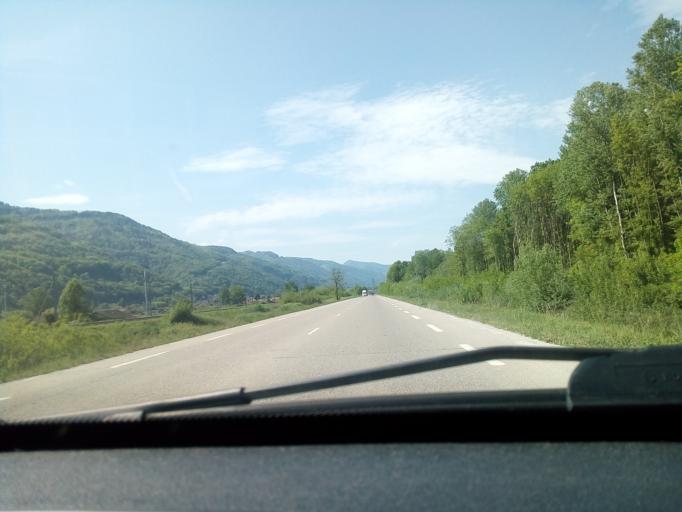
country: FR
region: Rhone-Alpes
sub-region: Departement de l'Isere
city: Froges
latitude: 45.2753
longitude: 5.9173
